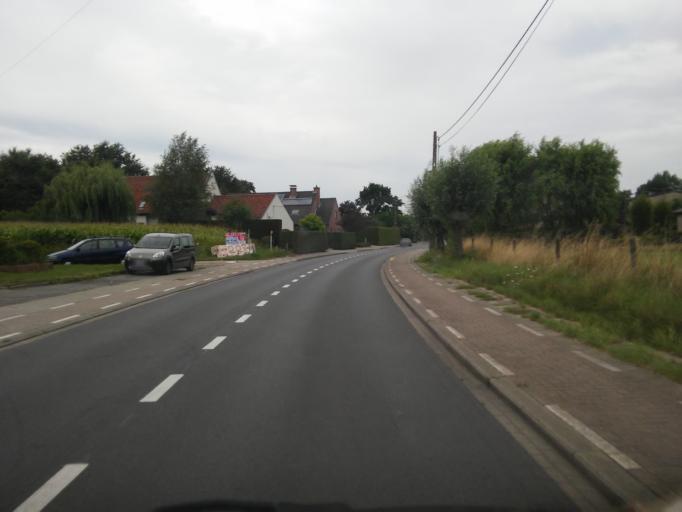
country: BE
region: Flanders
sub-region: Provincie Oost-Vlaanderen
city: Buggenhout
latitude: 51.0210
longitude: 4.1955
